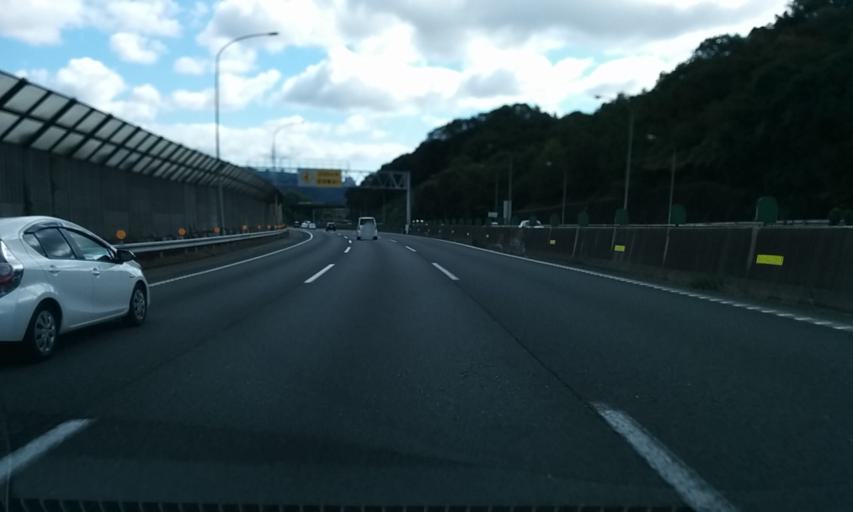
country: JP
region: Hyogo
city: Takarazuka
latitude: 34.8278
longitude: 135.2978
